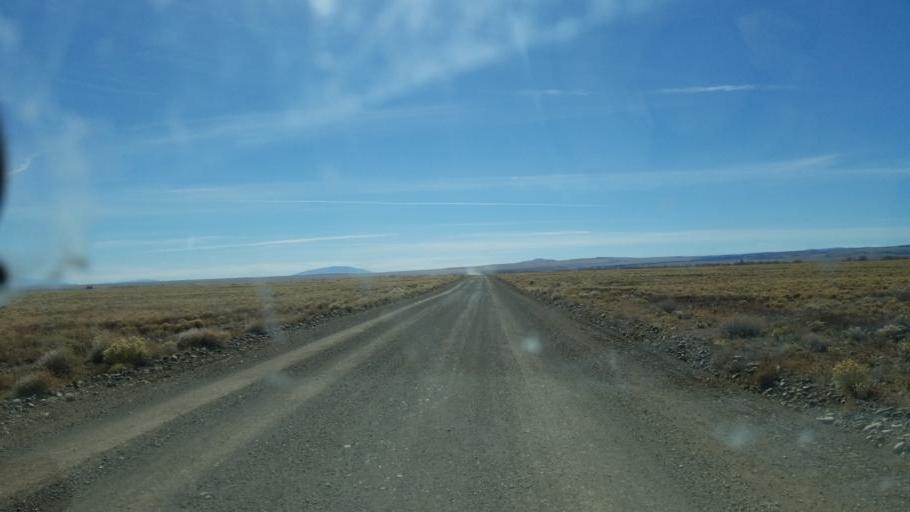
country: US
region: Colorado
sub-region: Rio Grande County
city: Monte Vista
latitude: 37.3312
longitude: -106.1489
